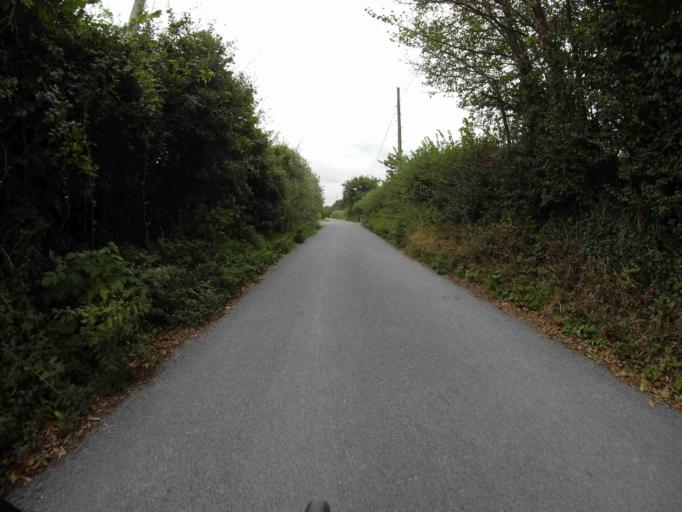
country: GB
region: England
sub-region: Devon
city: Topsham
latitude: 50.6936
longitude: -3.4707
